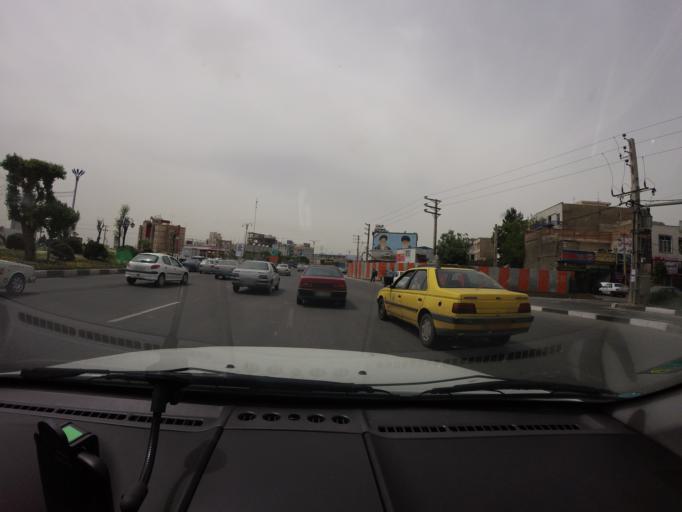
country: IR
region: Tehran
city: Eslamshahr
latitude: 35.5619
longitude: 51.2534
